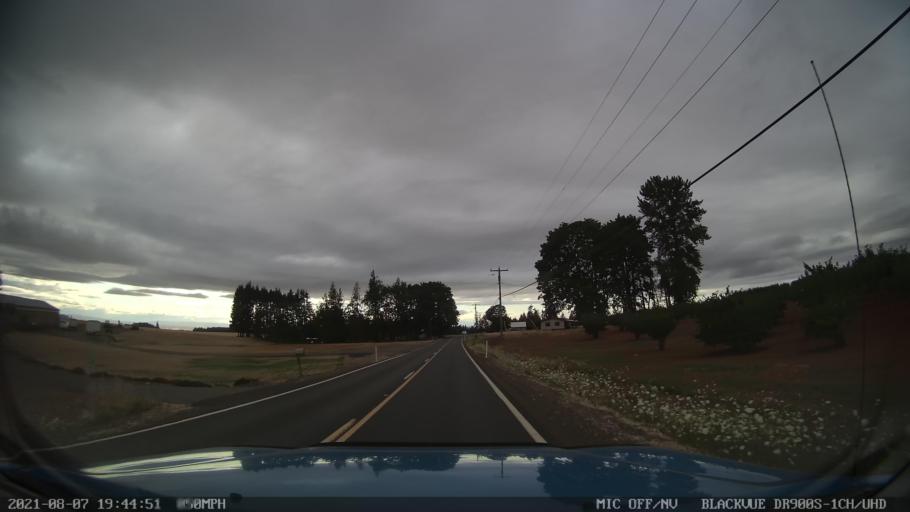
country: US
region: Oregon
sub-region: Marion County
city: Silverton
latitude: 44.9429
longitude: -122.6887
